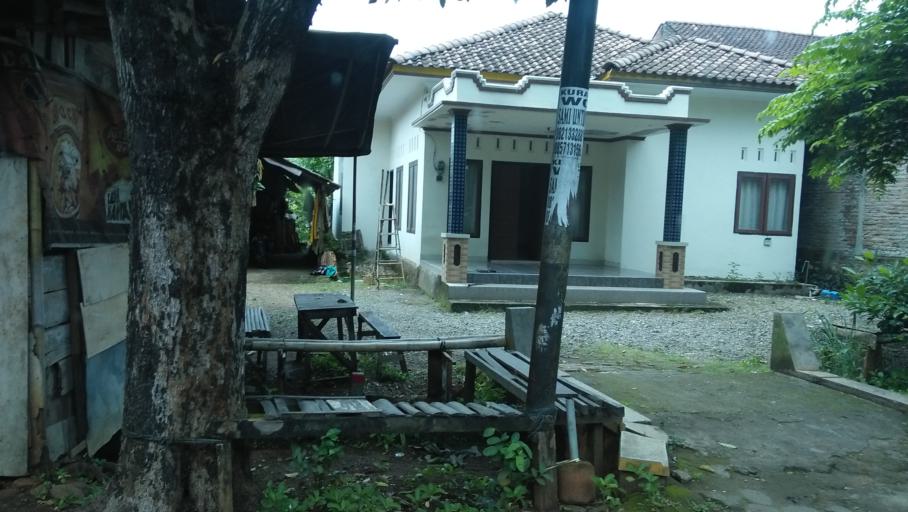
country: ID
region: Central Java
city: Mlonggo
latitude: -6.5640
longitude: 110.6633
